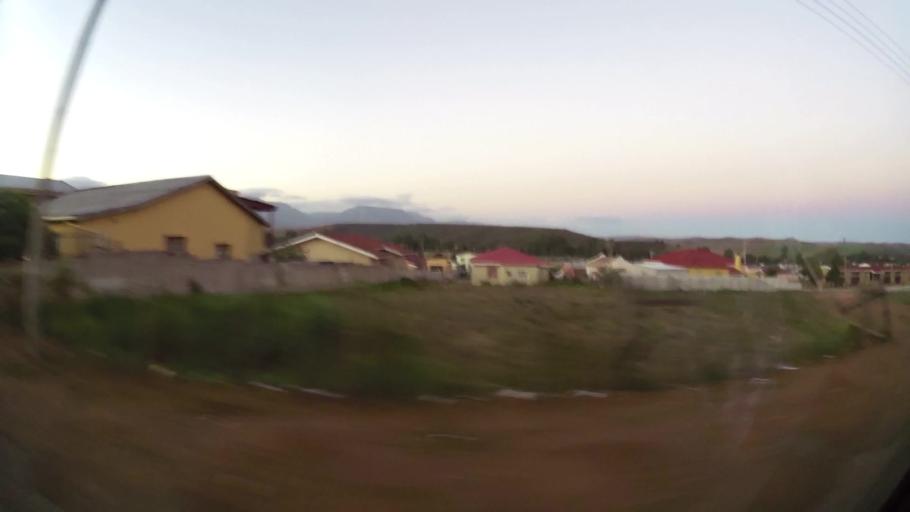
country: ZA
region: Western Cape
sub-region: Eden District Municipality
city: Riversdale
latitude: -34.1011
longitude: 21.2665
